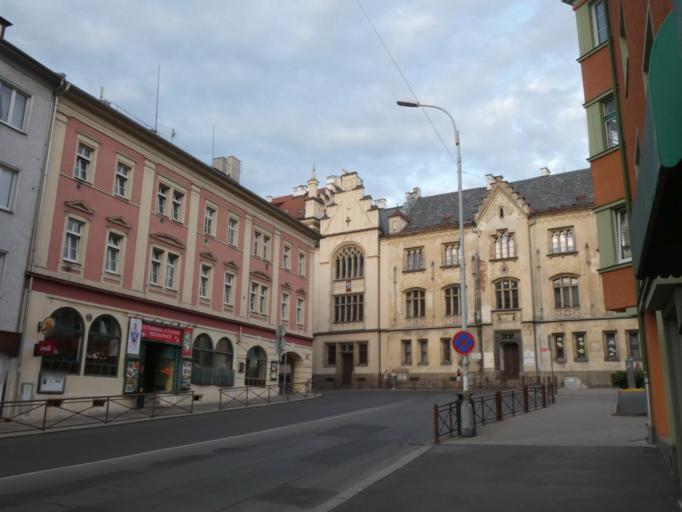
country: CZ
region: Ustecky
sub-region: Okres Decin
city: Decin
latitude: 50.7803
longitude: 14.2117
